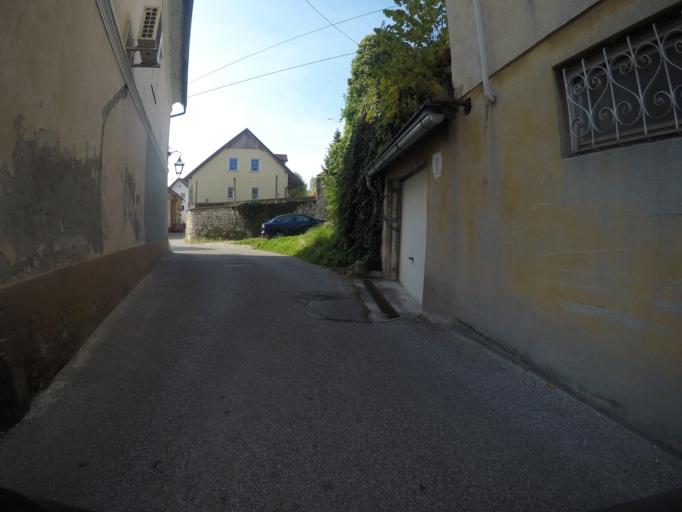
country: SI
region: Kamnik
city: Kamnik
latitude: 46.2235
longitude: 14.6100
